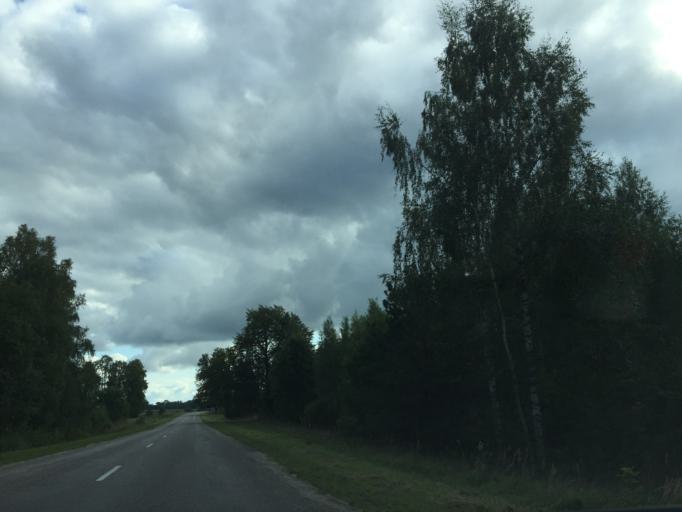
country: LV
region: Limbazu Rajons
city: Limbazi
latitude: 57.3922
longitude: 24.6897
